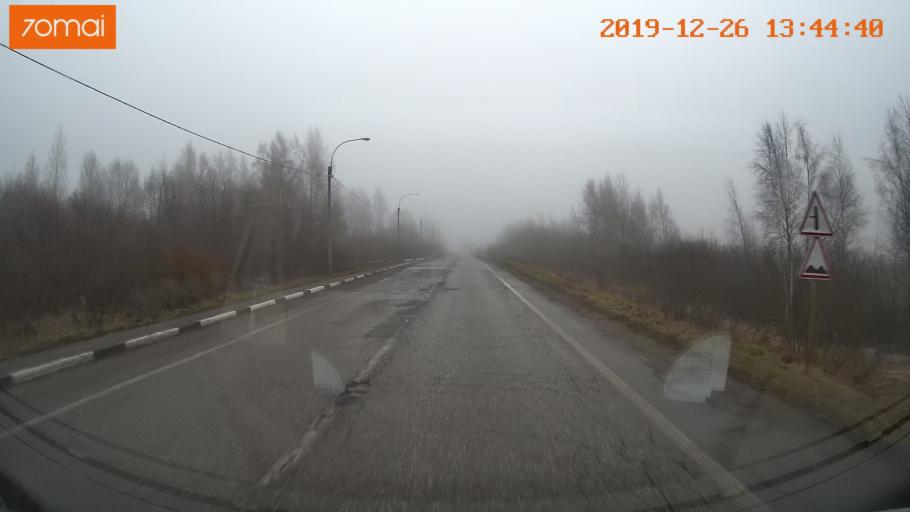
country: RU
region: Vologda
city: Sheksna
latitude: 58.7002
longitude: 38.5094
